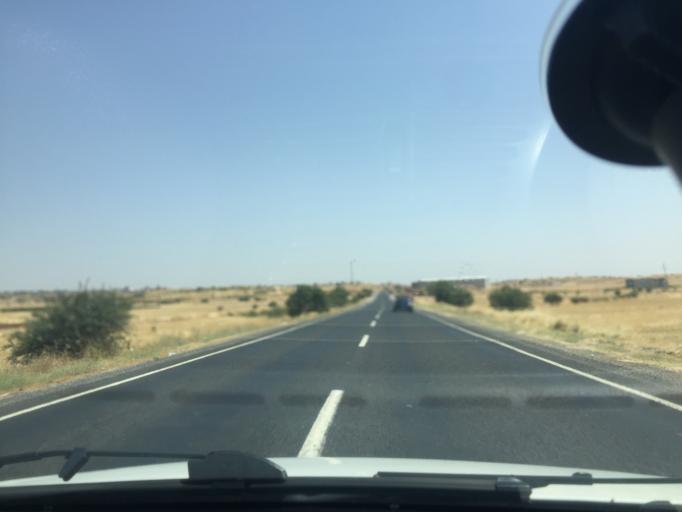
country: TR
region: Mardin
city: Acirli
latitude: 37.4491
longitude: 41.2704
